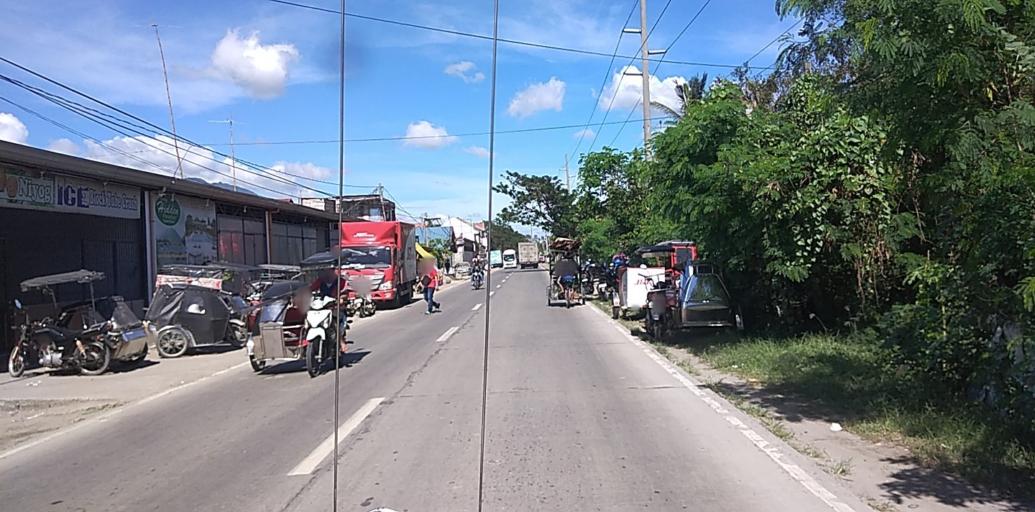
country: PH
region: Central Luzon
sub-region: Province of Pampanga
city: Arayat
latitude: 15.1238
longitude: 120.7758
